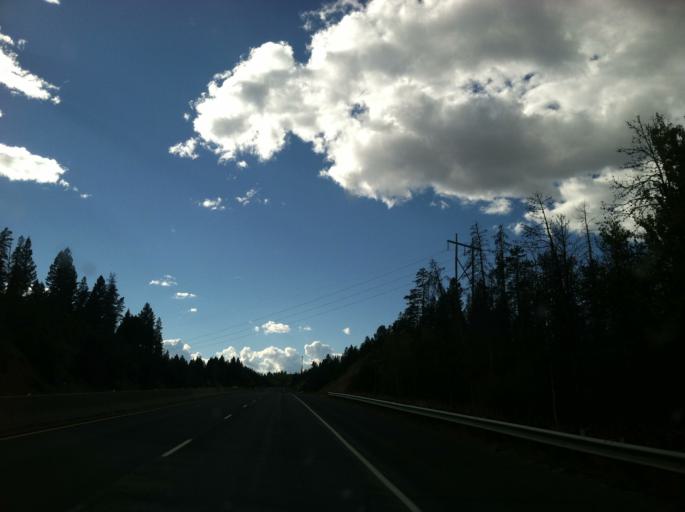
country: US
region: Montana
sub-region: Silver Bow County
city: Butte
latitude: 45.9173
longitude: -112.3980
